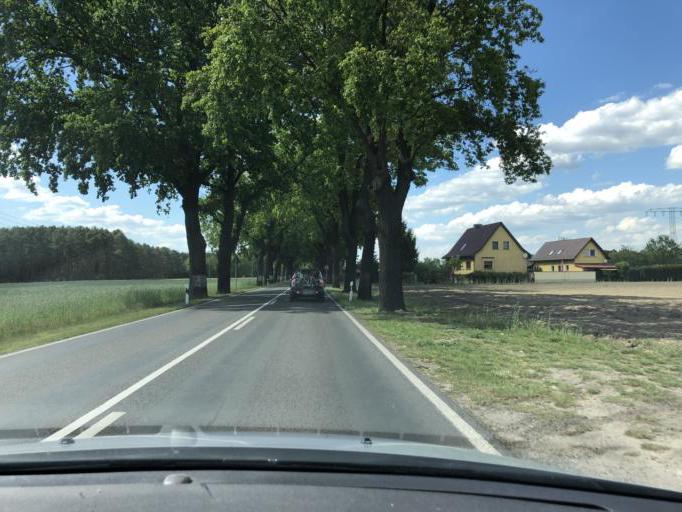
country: DE
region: Brandenburg
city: Storkow
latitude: 52.2683
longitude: 13.9260
